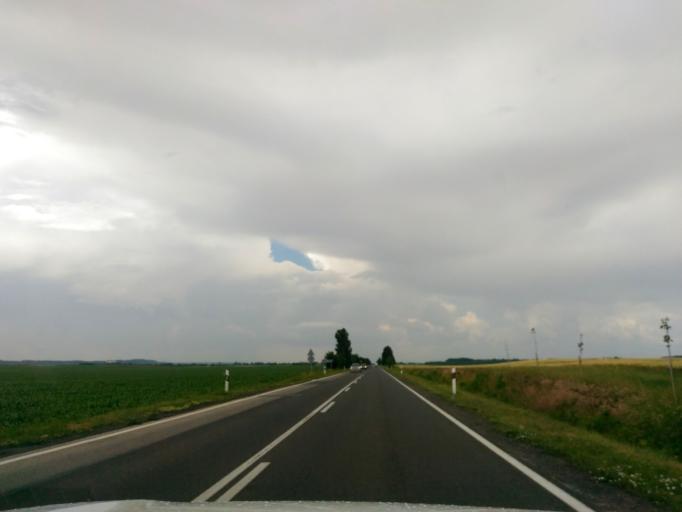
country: HU
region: Tolna
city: Fadd
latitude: 46.4855
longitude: 18.7859
